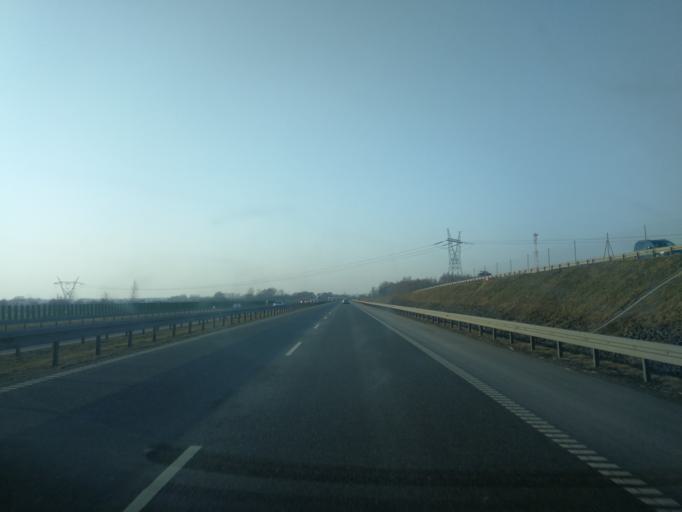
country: PL
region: Warmian-Masurian Voivodeship
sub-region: Powiat elblaski
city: Gronowo Gorne
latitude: 54.1181
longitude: 19.4747
